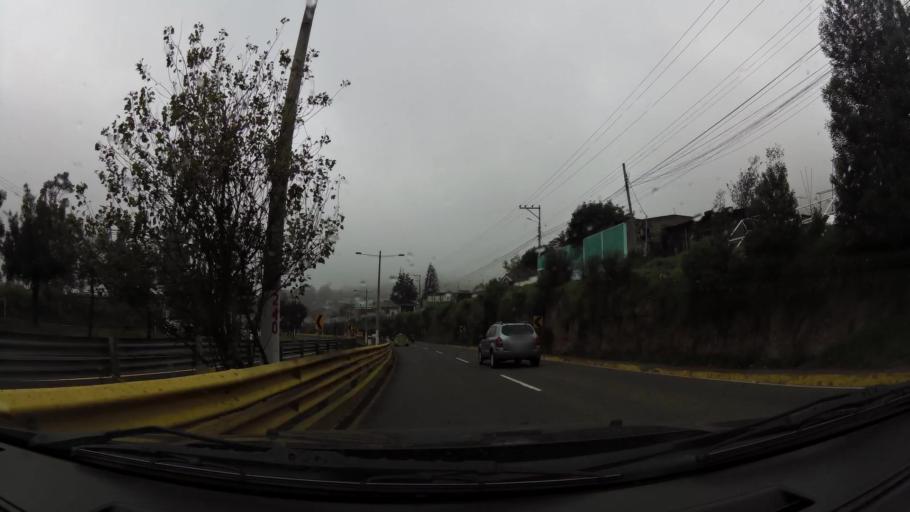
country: EC
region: Pichincha
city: Quito
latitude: -0.2718
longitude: -78.4903
